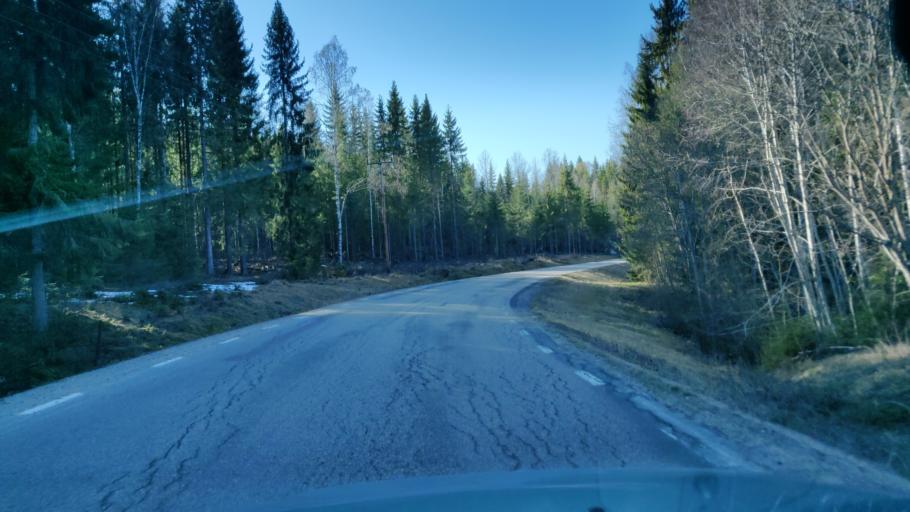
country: SE
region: Vaermland
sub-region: Munkfors Kommun
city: Munkfors
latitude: 59.9706
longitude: 13.4185
